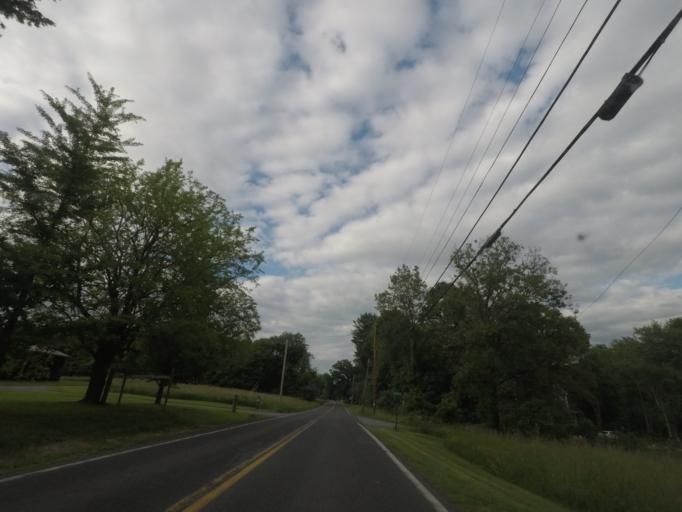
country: US
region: New York
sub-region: Ulster County
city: Plattekill
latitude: 41.6142
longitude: -74.1085
